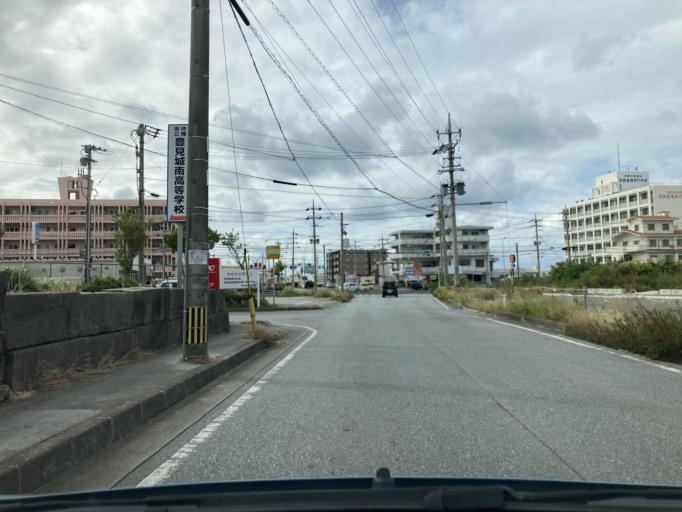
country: JP
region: Okinawa
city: Tomigusuku
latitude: 26.1621
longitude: 127.6702
